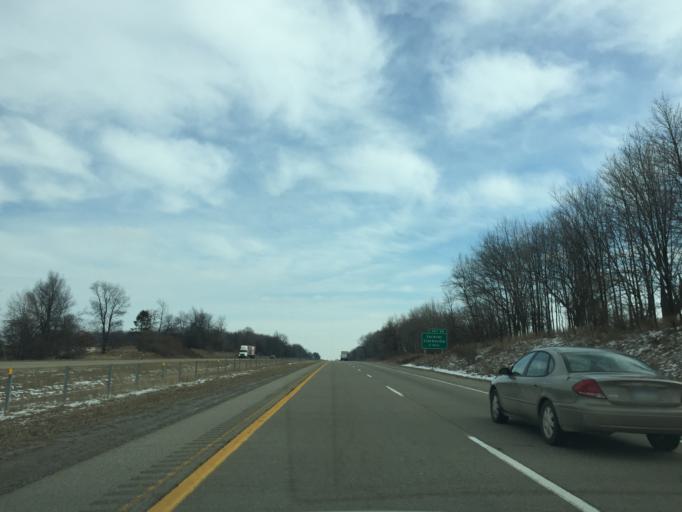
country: US
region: Michigan
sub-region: Ionia County
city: Saranac
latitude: 42.8793
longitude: -85.2693
